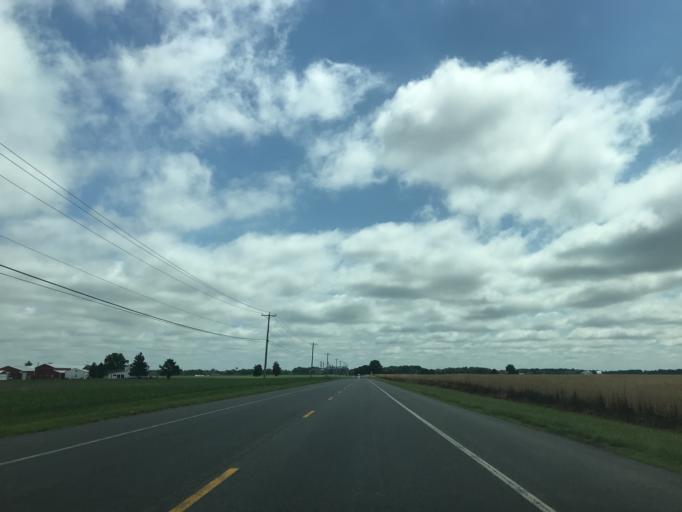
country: US
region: Maryland
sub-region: Caroline County
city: Ridgely
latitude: 38.9315
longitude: -75.9056
